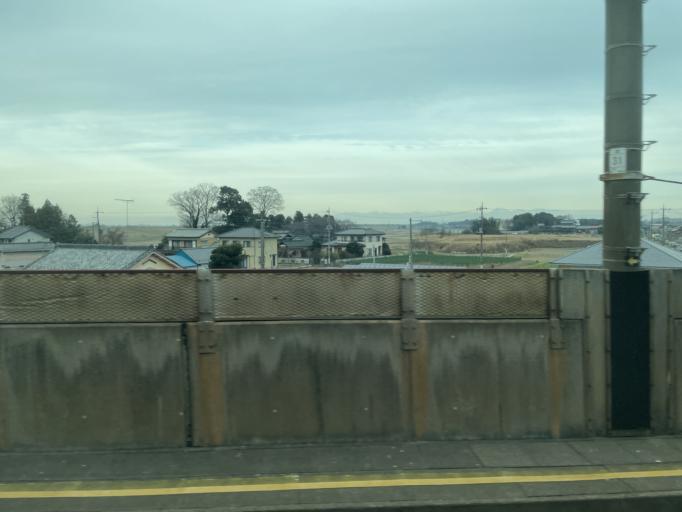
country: JP
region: Saitama
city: Kurihashi
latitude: 36.1513
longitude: 139.7073
